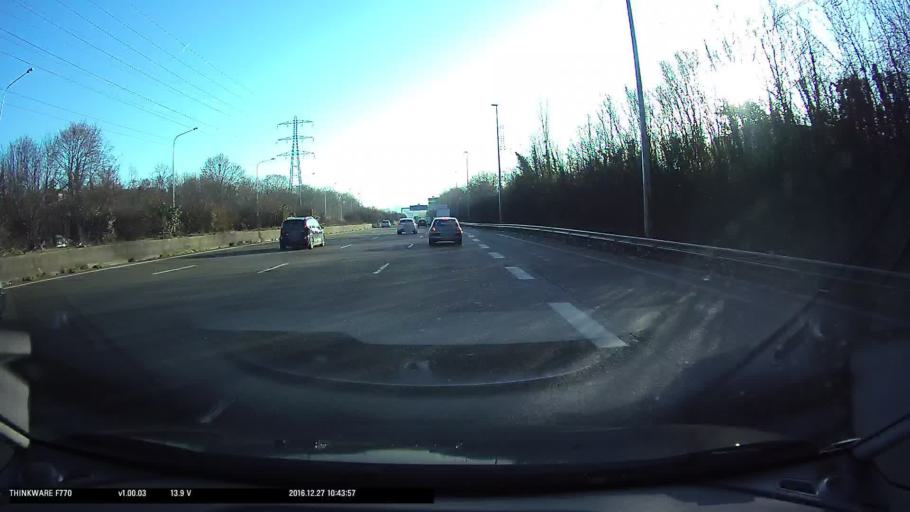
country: FR
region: Ile-de-France
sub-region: Departement du Val-d'Oise
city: Cergy-Pontoise
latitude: 49.0383
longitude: 2.0875
